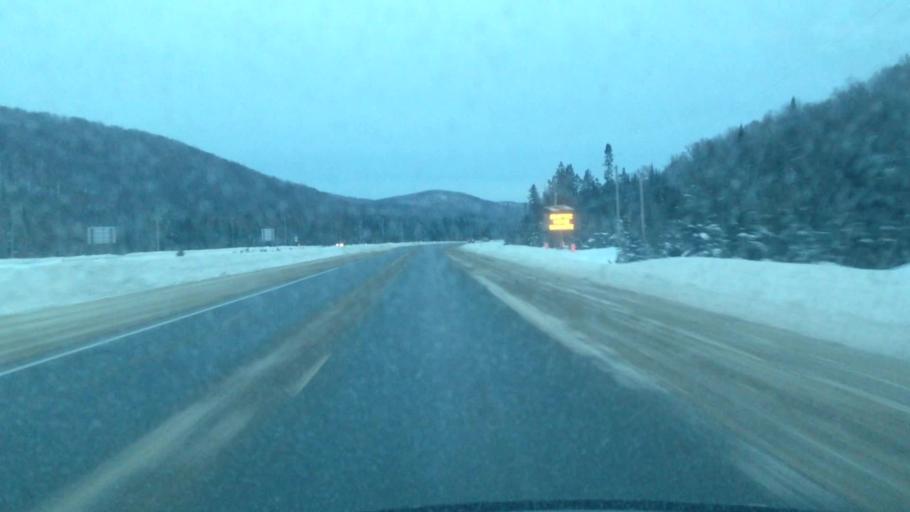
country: CA
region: Quebec
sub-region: Laurentides
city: Mont-Tremblant
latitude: 46.1231
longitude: -74.4500
